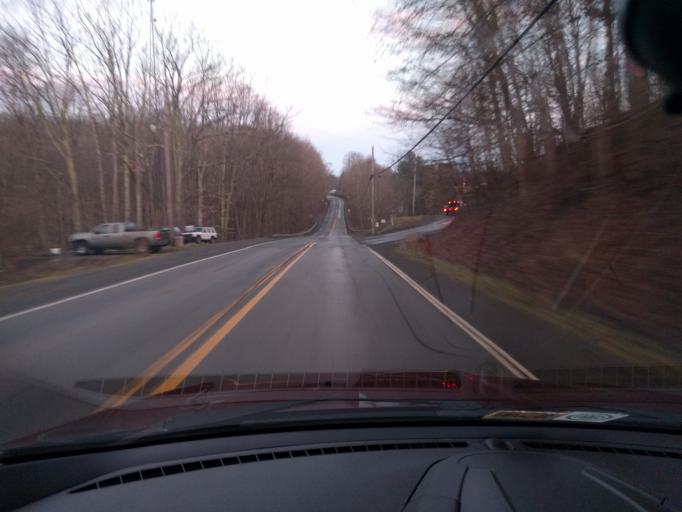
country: US
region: West Virginia
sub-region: Greenbrier County
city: Rainelle
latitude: 38.0090
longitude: -80.8800
